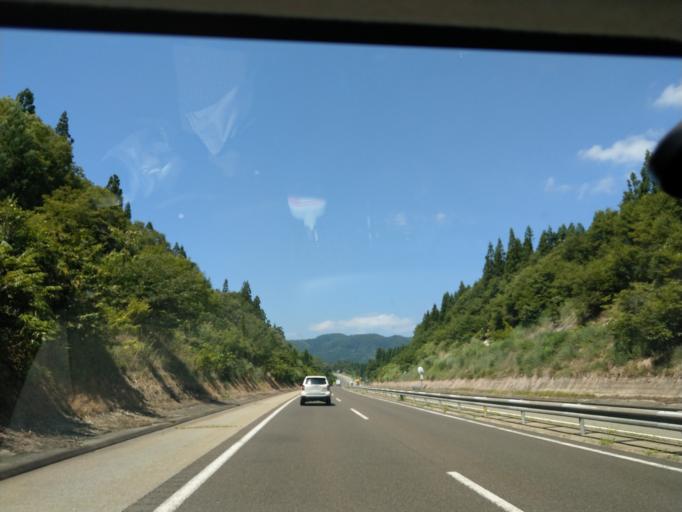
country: JP
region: Akita
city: Omagari
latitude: 39.4146
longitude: 140.4379
